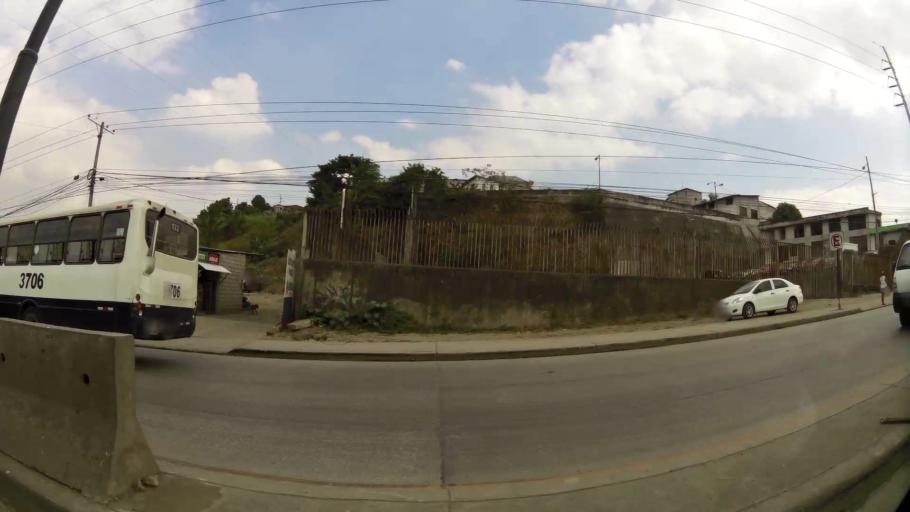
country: EC
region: Guayas
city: Santa Lucia
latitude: -2.1188
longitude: -79.9641
